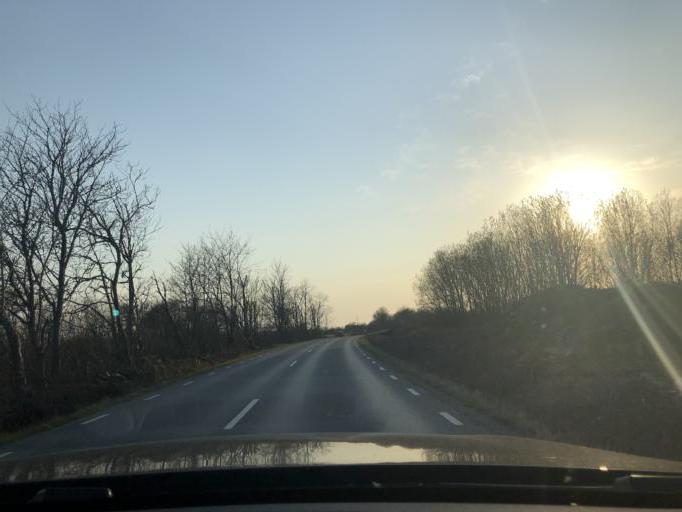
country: SE
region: Kalmar
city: Faerjestaden
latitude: 56.6540
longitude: 16.5386
